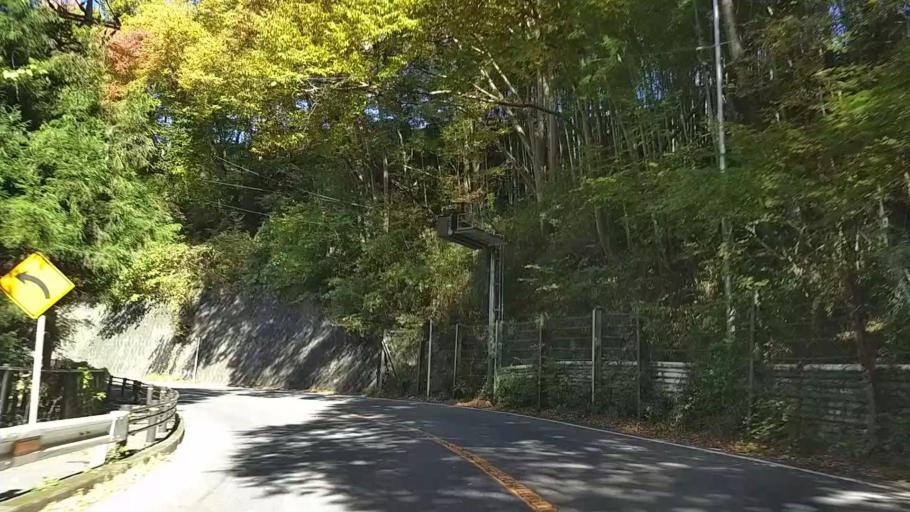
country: JP
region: Yamanashi
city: Uenohara
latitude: 35.6190
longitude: 139.1309
